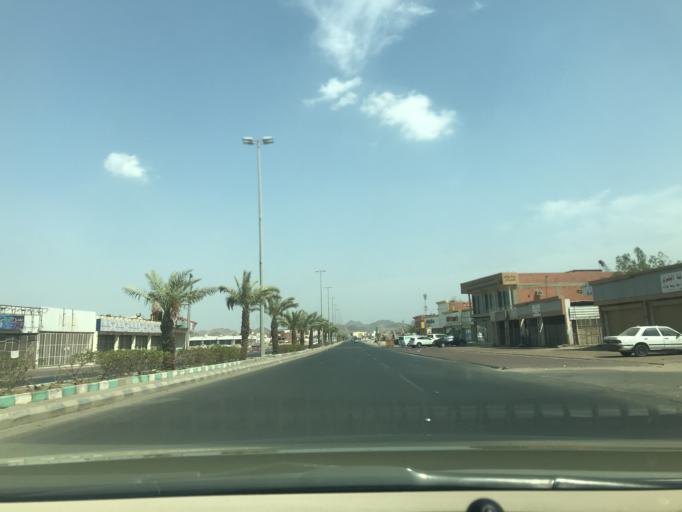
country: SA
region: Makkah
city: Al Jumum
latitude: 21.6223
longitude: 39.6835
